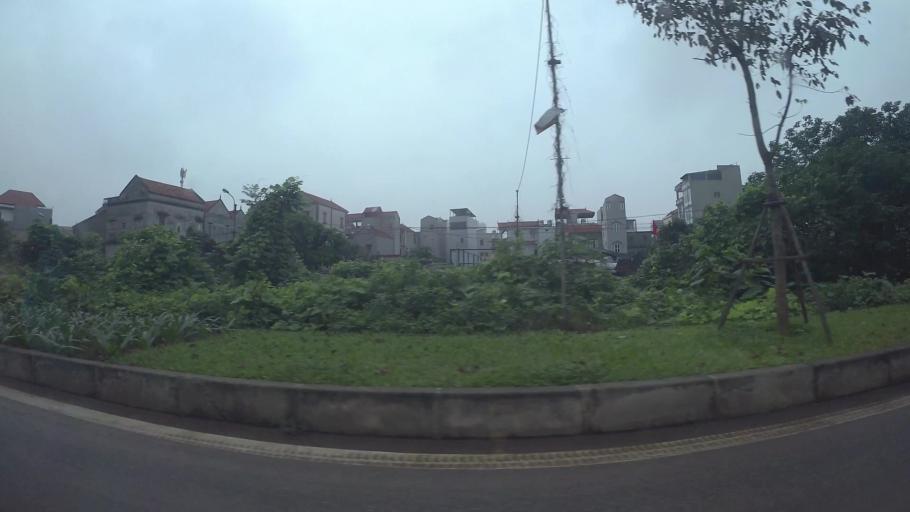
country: VN
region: Ha Noi
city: Van Dien
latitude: 20.9704
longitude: 105.8733
